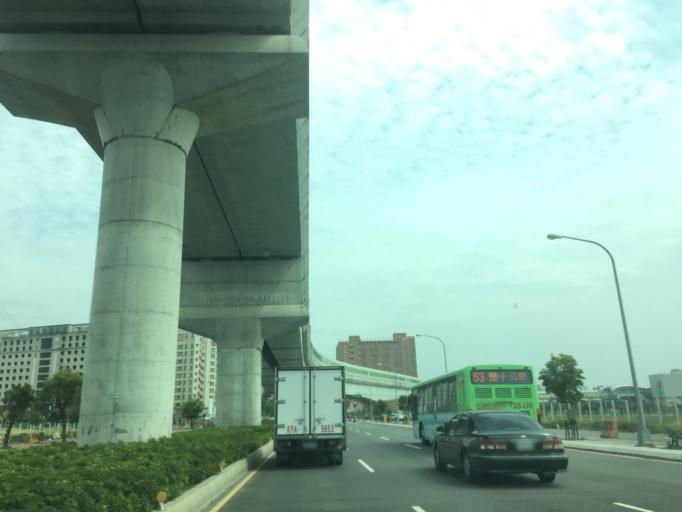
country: TW
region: Taiwan
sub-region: Taichung City
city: Taichung
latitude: 24.1245
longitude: 120.6472
